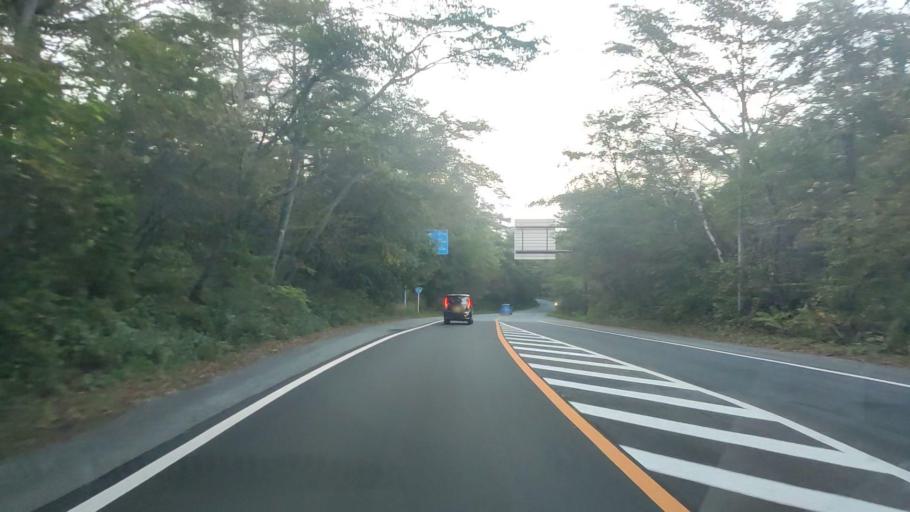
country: JP
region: Nagano
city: Komoro
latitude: 36.4053
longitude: 138.5696
